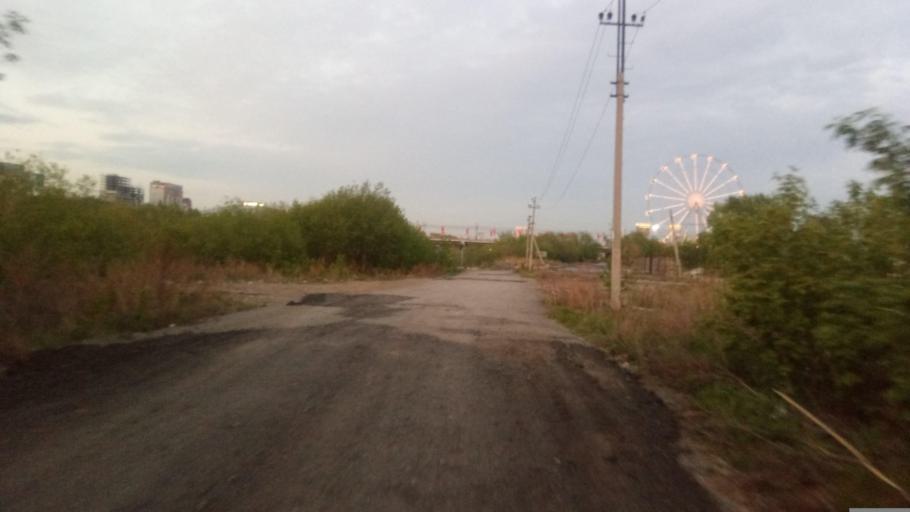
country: RU
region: Chelyabinsk
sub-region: Gorod Chelyabinsk
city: Chelyabinsk
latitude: 55.1713
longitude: 61.3828
